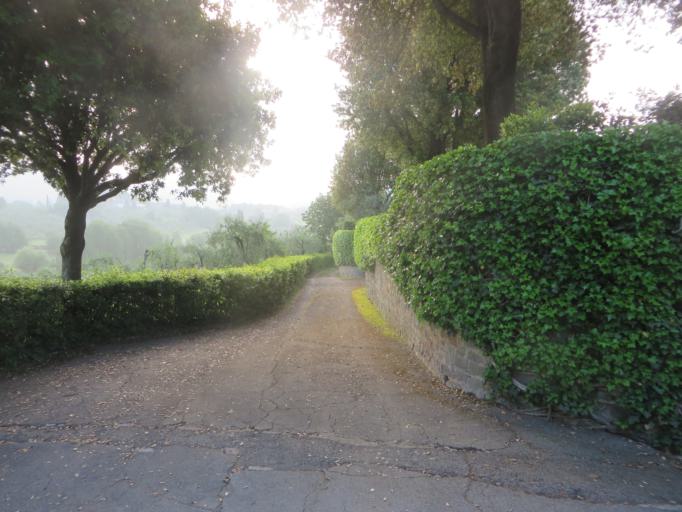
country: IT
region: Tuscany
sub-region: Province of Florence
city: Bagno a Ripoli
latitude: 43.7452
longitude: 11.3226
